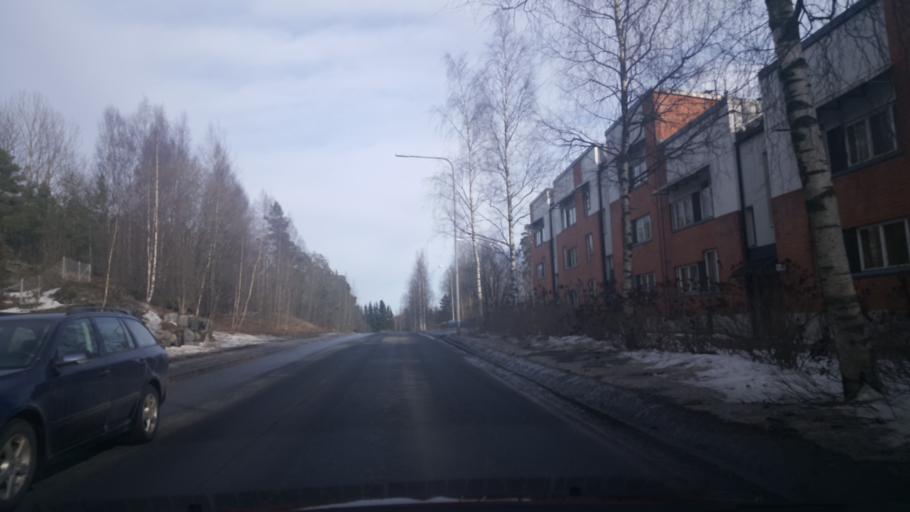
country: FI
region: Uusimaa
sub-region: Helsinki
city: Teekkarikylae
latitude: 60.2483
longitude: 24.8606
